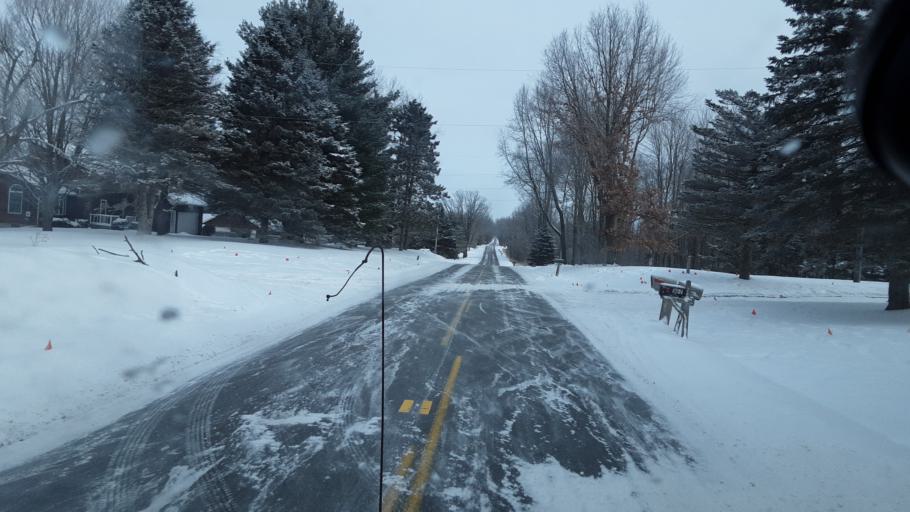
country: US
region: Michigan
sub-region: Jackson County
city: Jackson
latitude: 42.3258
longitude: -84.4828
